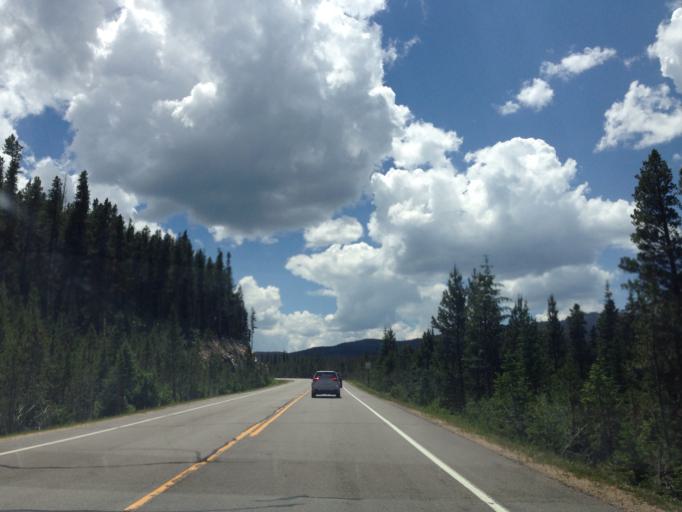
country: US
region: Colorado
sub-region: Larimer County
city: Estes Park
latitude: 40.6101
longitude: -105.8314
